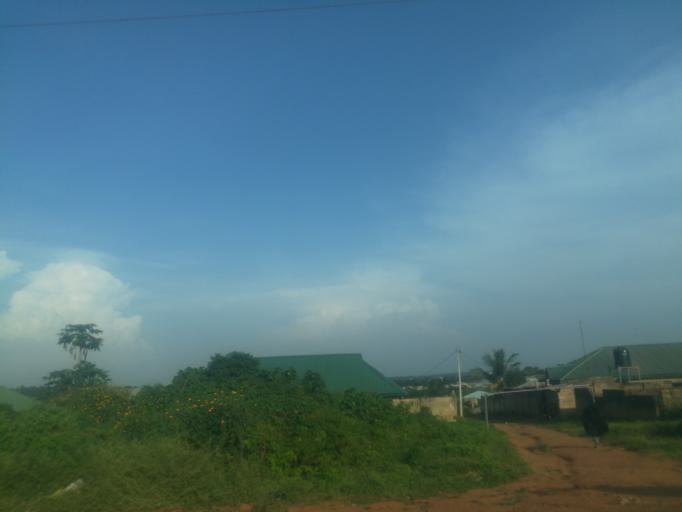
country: NG
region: Oyo
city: Moniya
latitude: 7.5660
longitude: 3.8861
